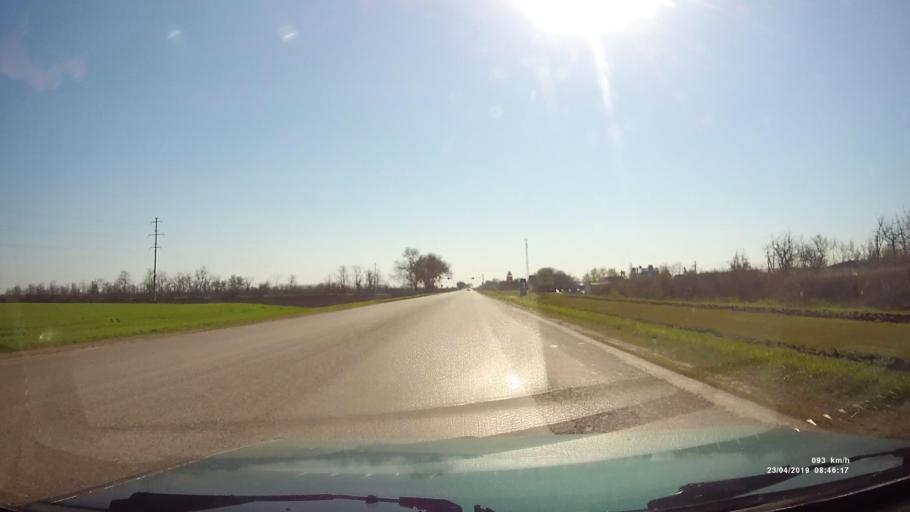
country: RU
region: Rostov
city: Gigant
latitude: 46.5174
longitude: 41.3471
